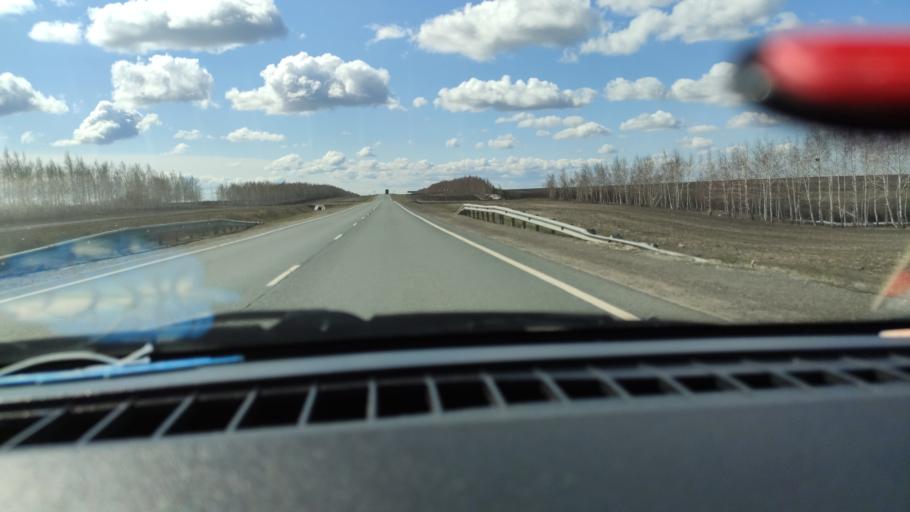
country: RU
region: Samara
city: Syzran'
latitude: 52.9110
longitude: 48.2996
